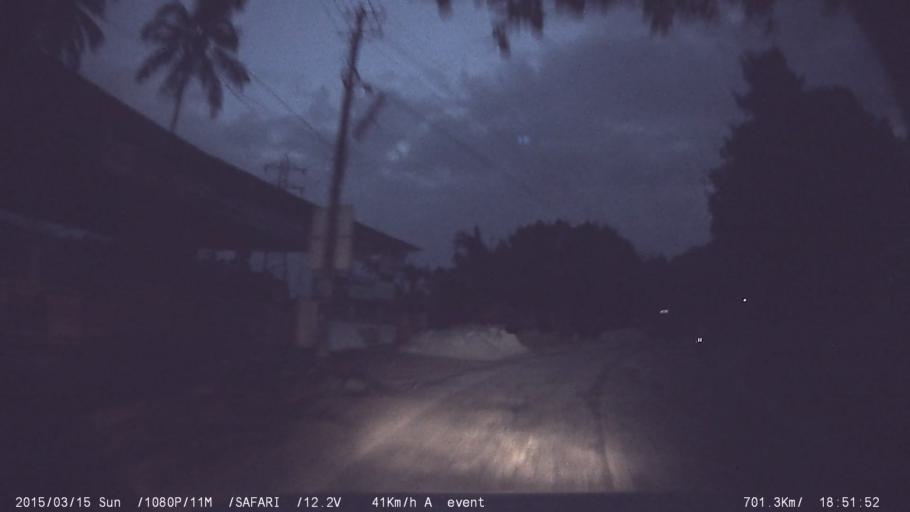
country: IN
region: Kerala
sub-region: Kottayam
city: Palackattumala
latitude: 9.8565
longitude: 76.6889
